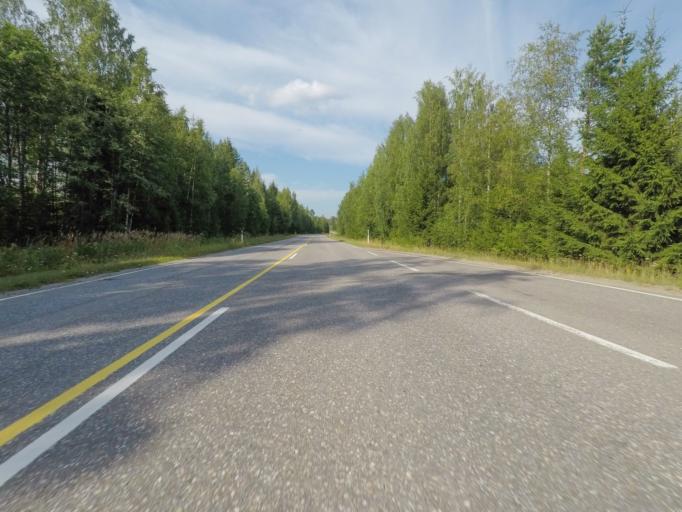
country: FI
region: Southern Savonia
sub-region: Savonlinna
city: Sulkava
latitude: 61.8187
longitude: 28.4372
